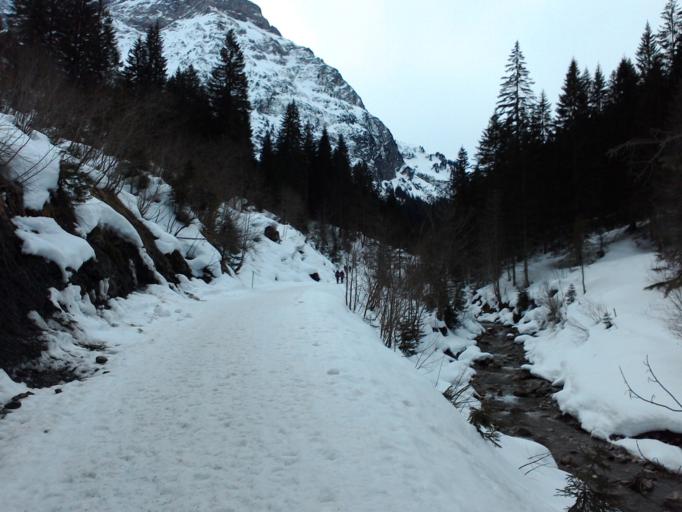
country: AT
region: Vorarlberg
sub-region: Politischer Bezirk Bregenz
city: Mittelberg
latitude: 47.3030
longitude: 10.1183
